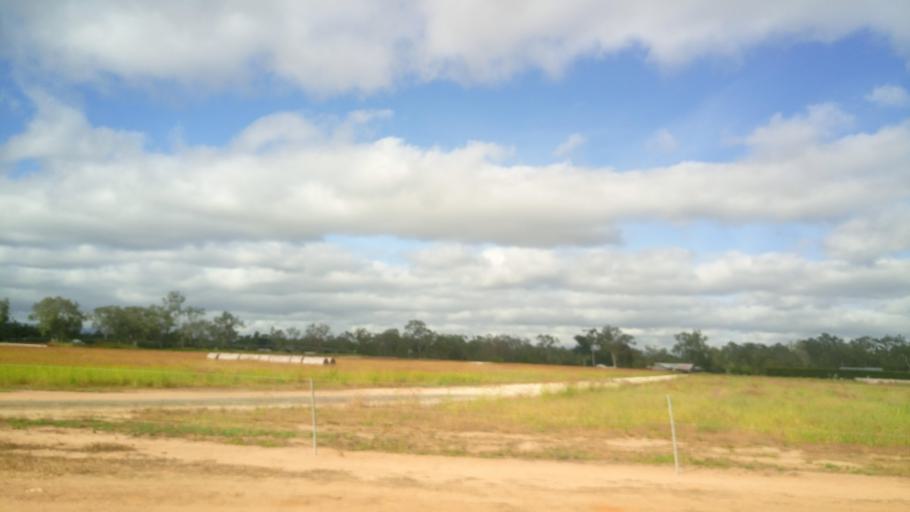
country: AU
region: Queensland
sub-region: Tablelands
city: Mareeba
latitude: -16.9790
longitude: 145.4723
